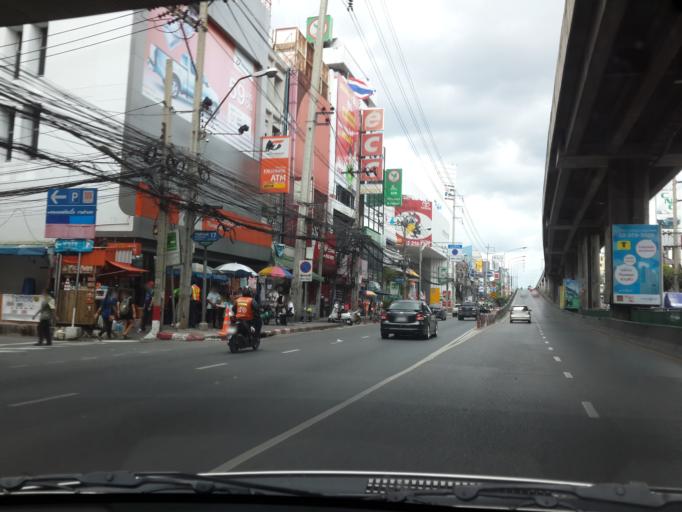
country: TH
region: Bangkok
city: Wang Thonglang
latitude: 13.7522
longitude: 100.6103
